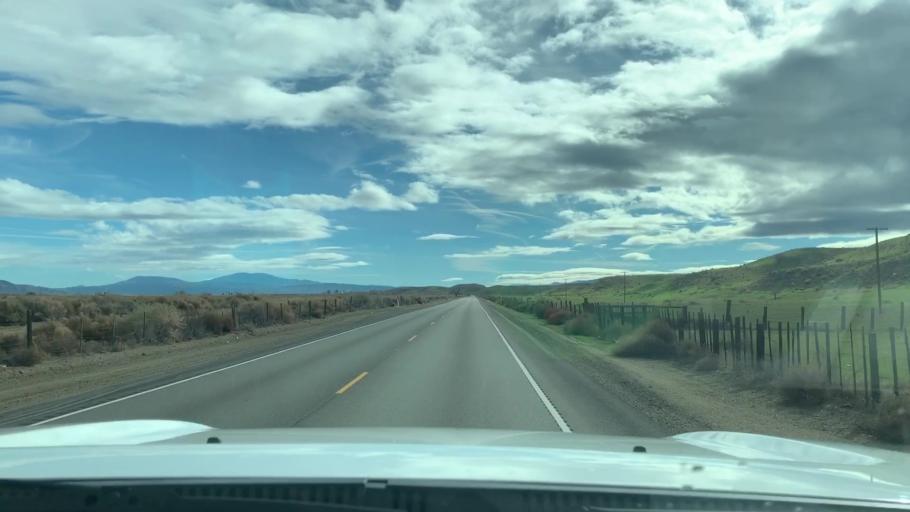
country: US
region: California
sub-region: Kern County
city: Taft Heights
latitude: 34.9760
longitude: -119.7552
